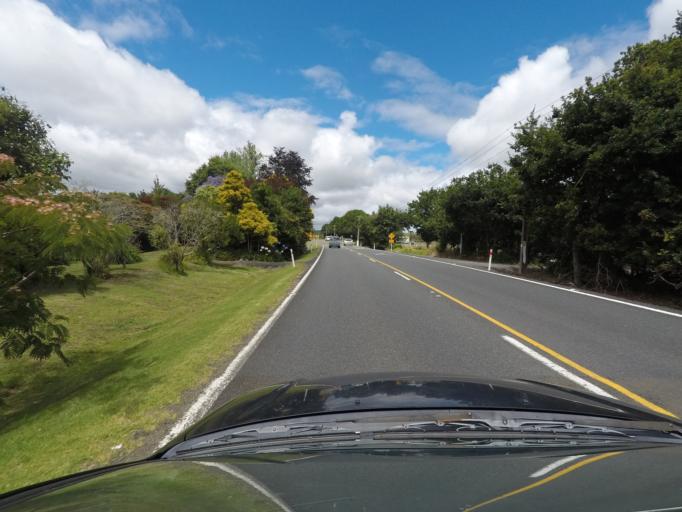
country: NZ
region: Northland
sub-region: Far North District
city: Kawakawa
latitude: -35.3626
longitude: 174.0903
